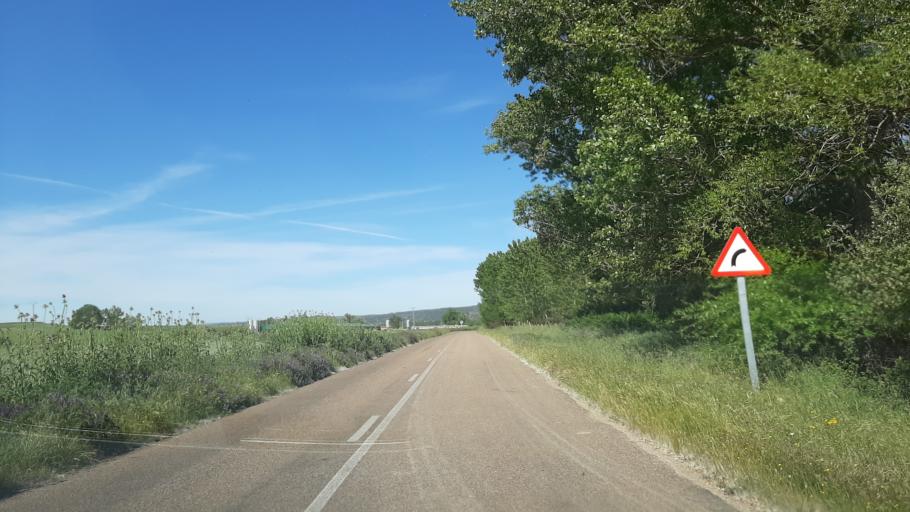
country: ES
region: Castille and Leon
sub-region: Provincia de Salamanca
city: Alba de Tormes
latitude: 40.8206
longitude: -5.4839
